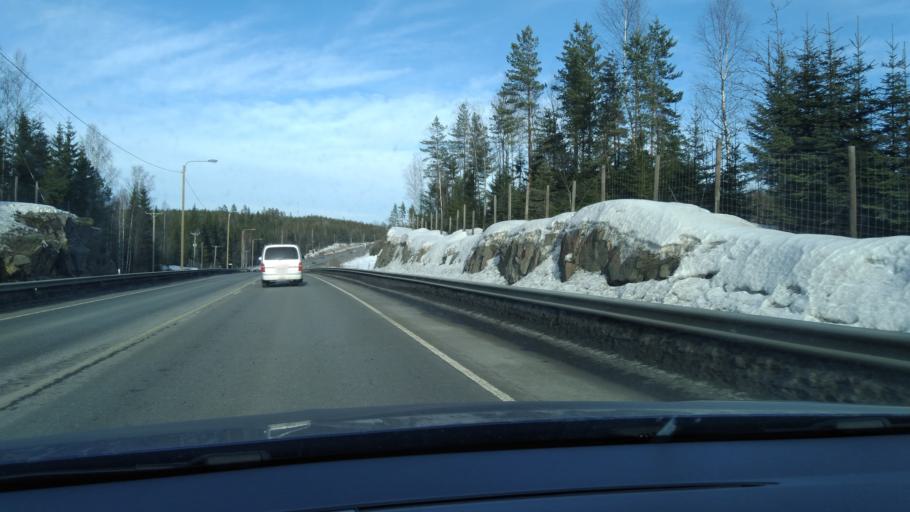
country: FI
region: Pirkanmaa
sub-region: Tampere
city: Orivesi
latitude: 61.6734
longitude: 24.2991
